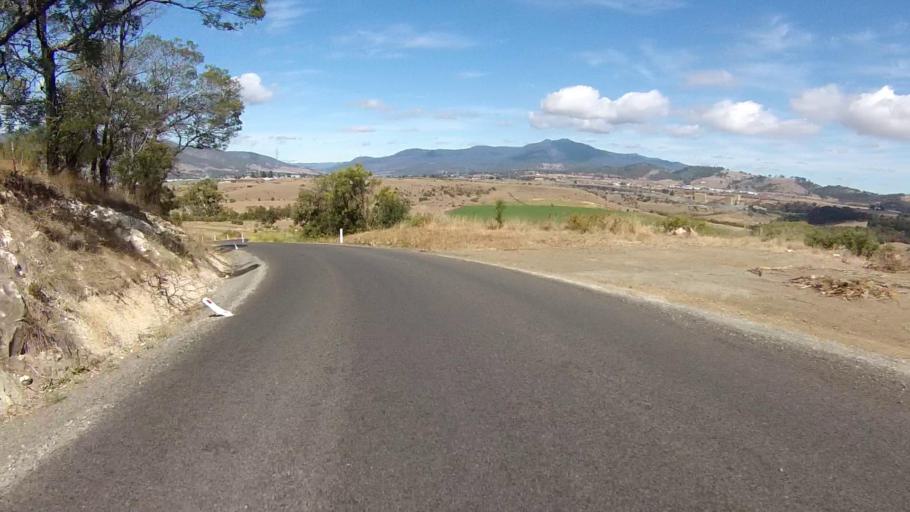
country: AU
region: Tasmania
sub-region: Brighton
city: Bridgewater
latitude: -42.7252
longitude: 147.2662
